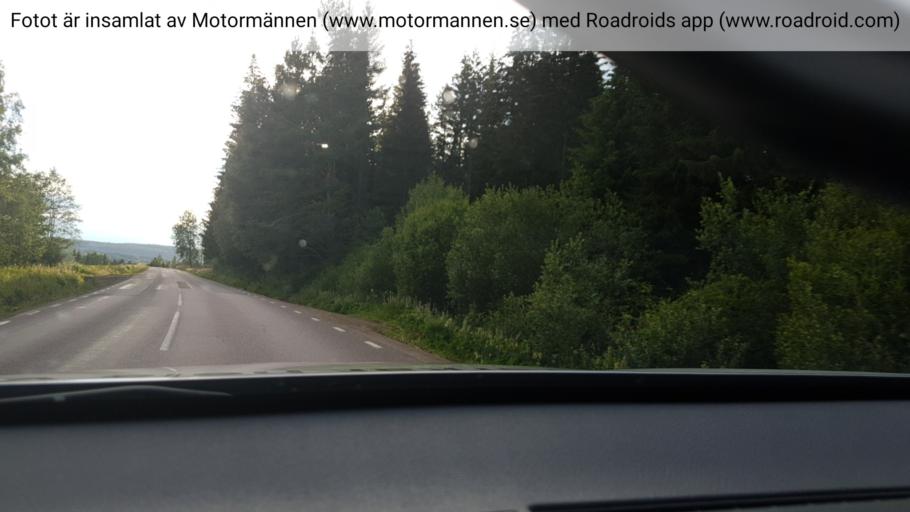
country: SE
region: Vaermland
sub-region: Sunne Kommun
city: Sunne
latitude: 59.8177
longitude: 13.1807
